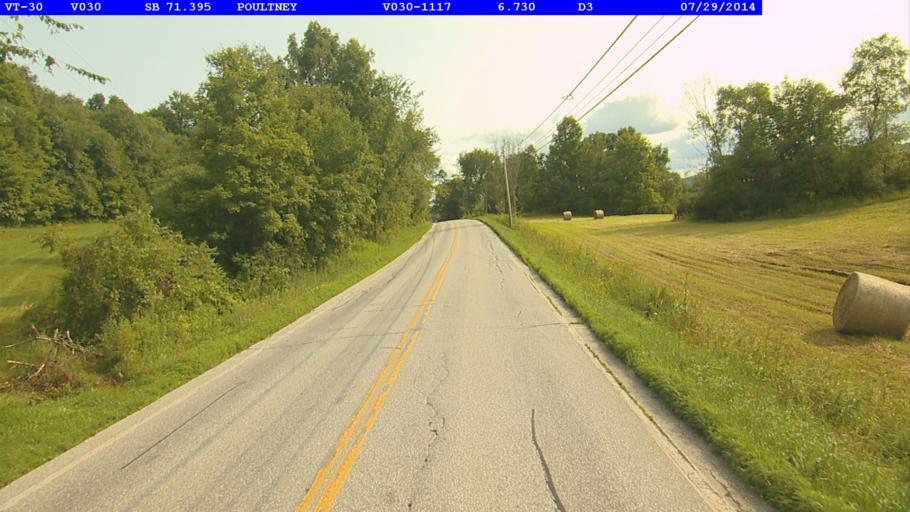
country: US
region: Vermont
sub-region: Rutland County
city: Poultney
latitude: 43.5479
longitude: -73.2270
